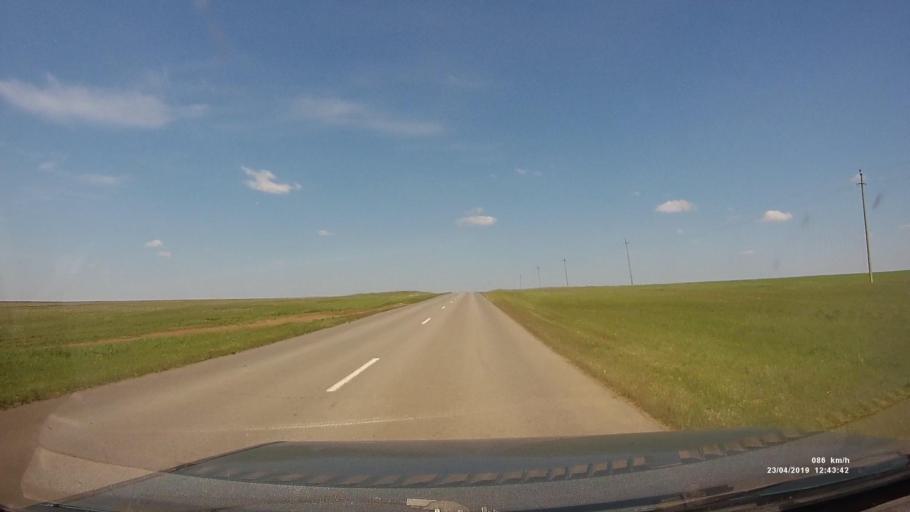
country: RU
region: Kalmykiya
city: Yashalta
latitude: 46.4673
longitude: 42.6501
